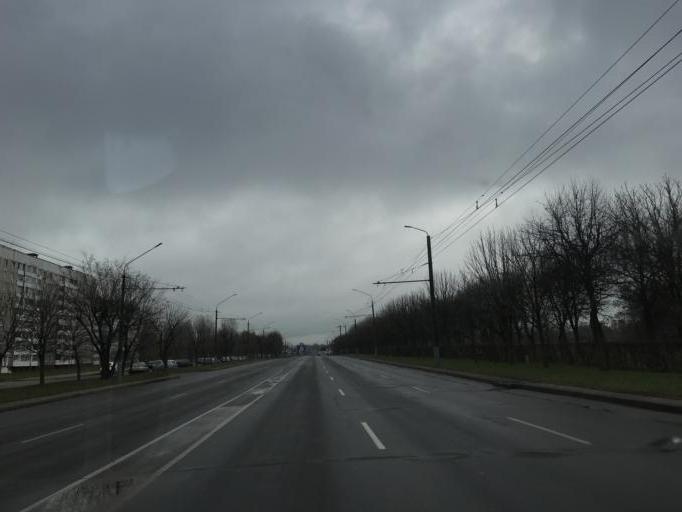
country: BY
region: Mogilev
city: Mahilyow
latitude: 53.8649
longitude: 30.3323
